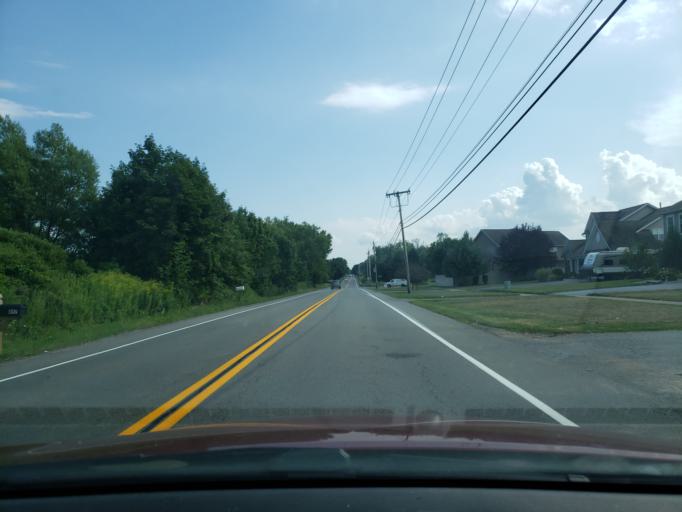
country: US
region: New York
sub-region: Monroe County
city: Greece
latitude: 43.2672
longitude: -77.7152
